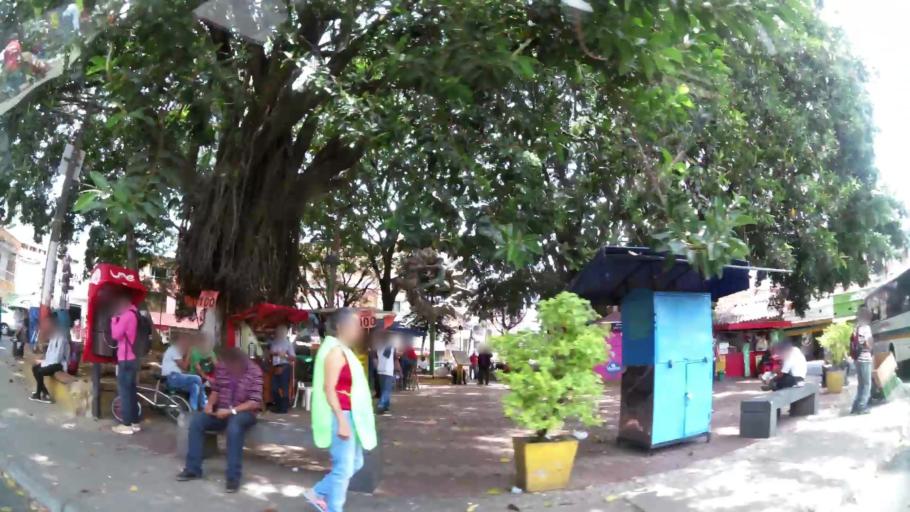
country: CO
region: Antioquia
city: Bello
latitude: 6.3357
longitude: -75.5553
